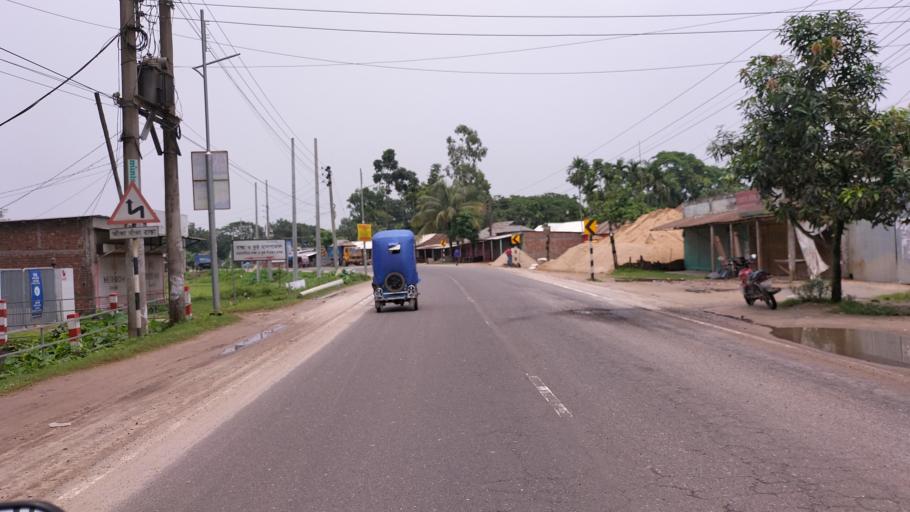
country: BD
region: Dhaka
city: Mymensingh
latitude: 24.7672
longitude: 90.4545
